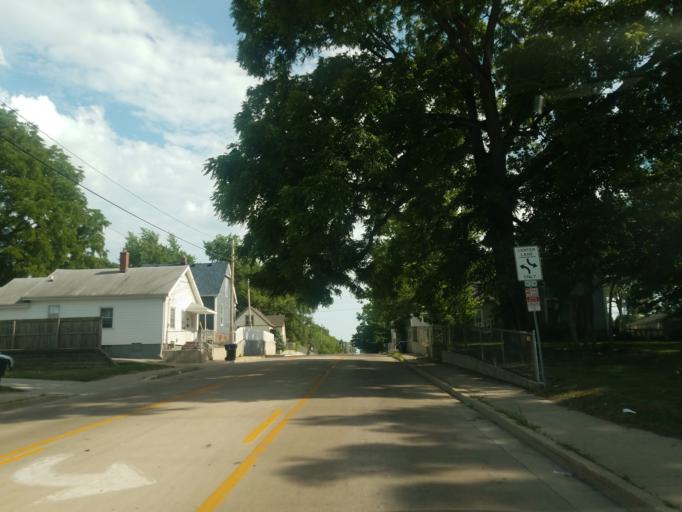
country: US
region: Illinois
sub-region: McLean County
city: Bloomington
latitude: 40.4783
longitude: -89.0067
